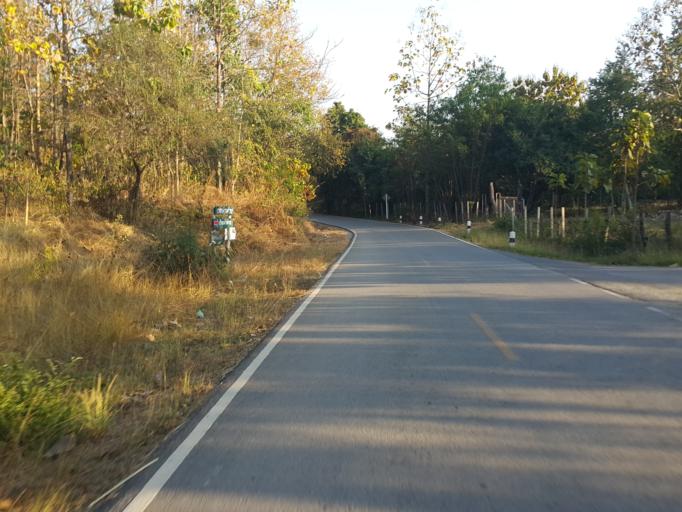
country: TH
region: Chiang Mai
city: Mae On
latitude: 18.7959
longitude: 99.2514
